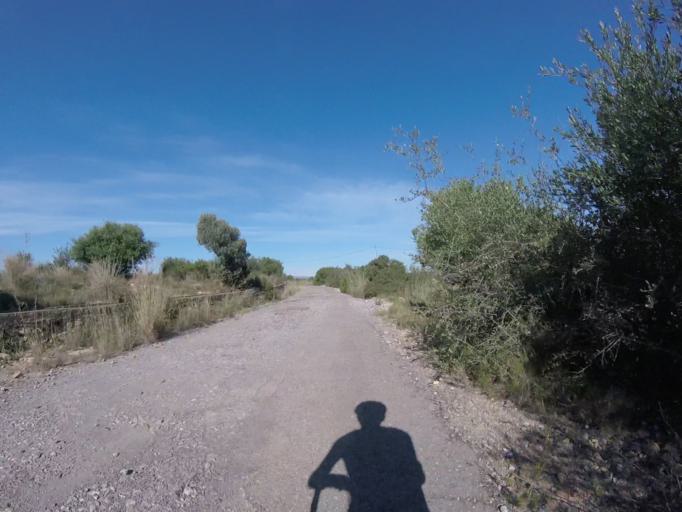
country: ES
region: Valencia
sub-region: Provincia de Castello
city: Torreblanca
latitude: 40.2084
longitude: 0.2409
